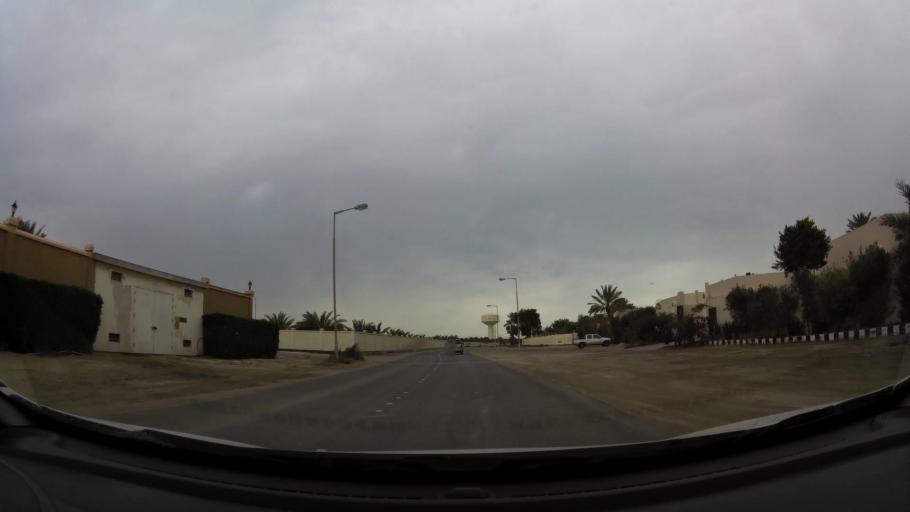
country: BH
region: Central Governorate
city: Madinat Hamad
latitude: 26.1368
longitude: 50.4632
